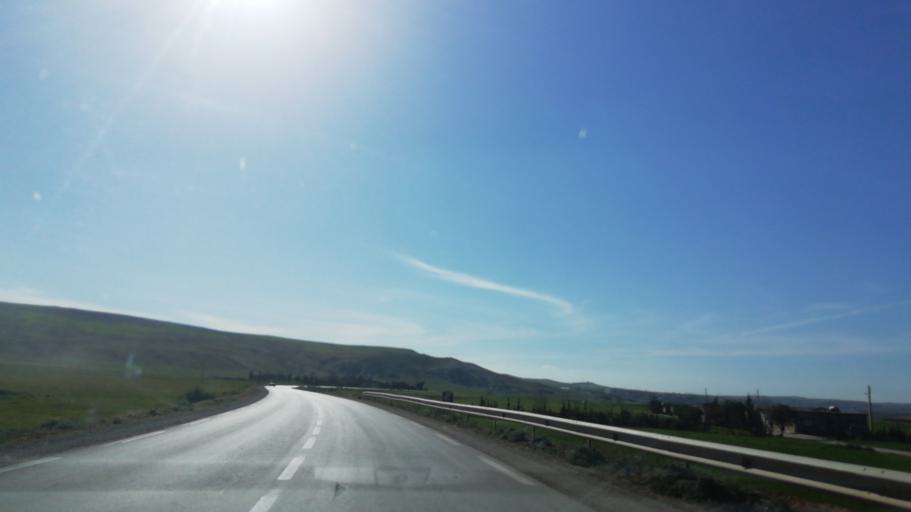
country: DZ
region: Mascara
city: Oued el Abtal
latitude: 35.4581
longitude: 0.7470
